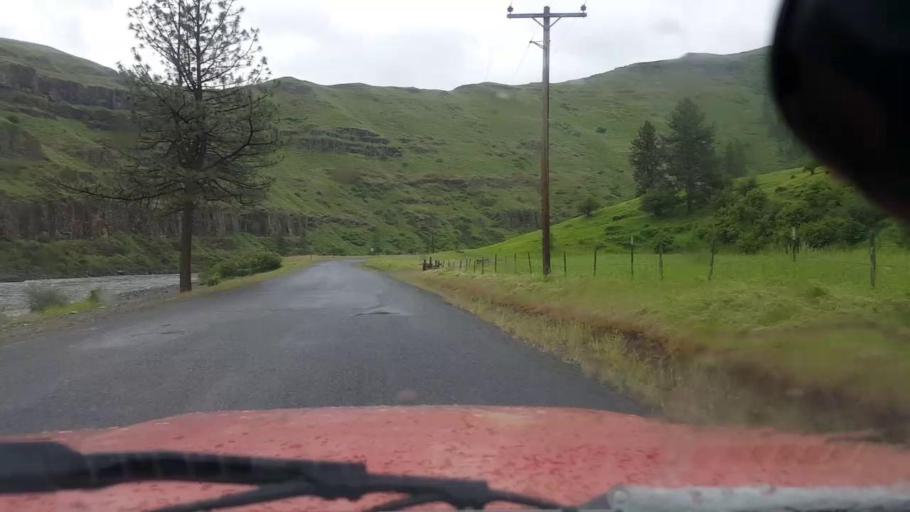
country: US
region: Washington
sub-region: Asotin County
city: Asotin
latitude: 46.0298
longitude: -117.3267
